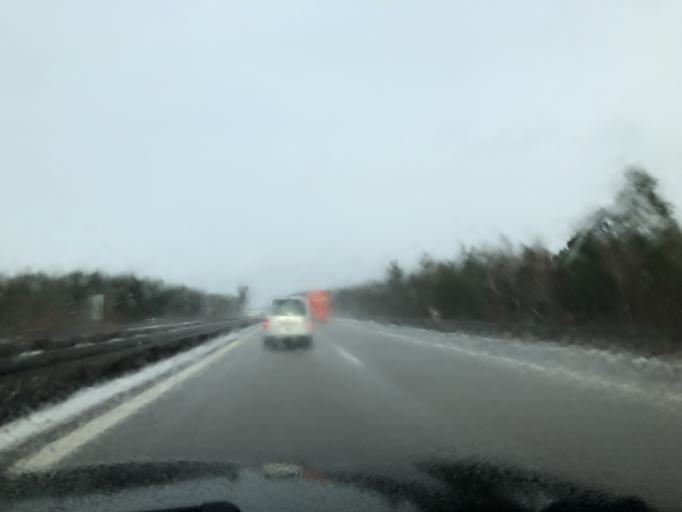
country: DE
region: Bavaria
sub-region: Upper Palatinate
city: Steinberg
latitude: 49.2929
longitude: 12.1454
